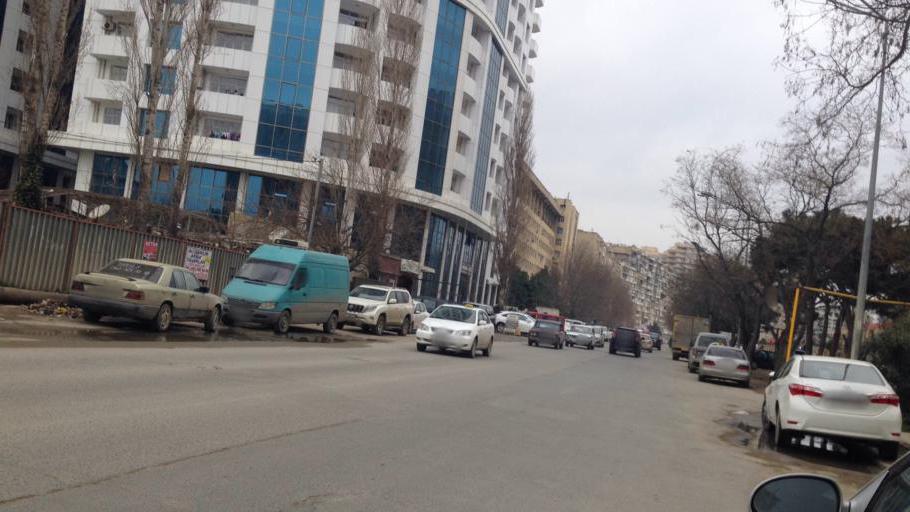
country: AZ
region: Baki
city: Badamdar
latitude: 40.3878
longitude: 49.8157
